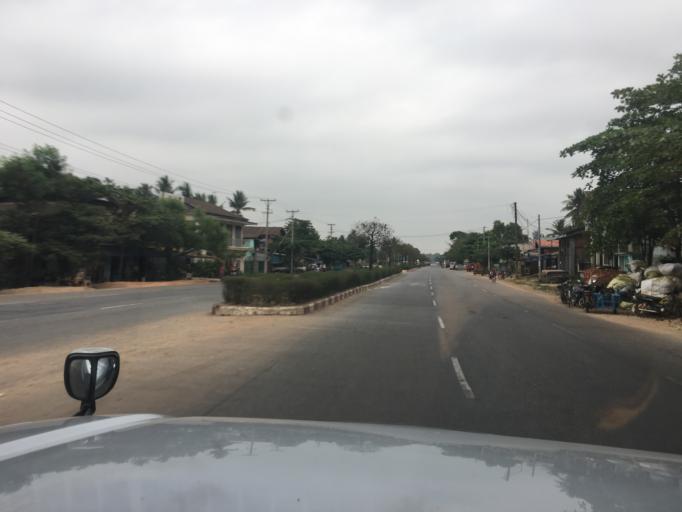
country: MM
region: Bago
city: Thanatpin
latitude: 17.1840
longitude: 96.3823
